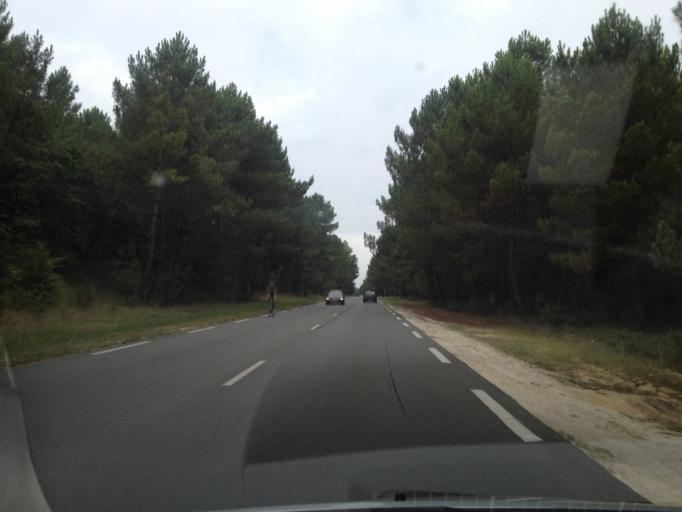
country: FR
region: Poitou-Charentes
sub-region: Departement de la Charente-Maritime
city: Saint-Palais-sur-Mer
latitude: 45.6615
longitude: -1.0802
